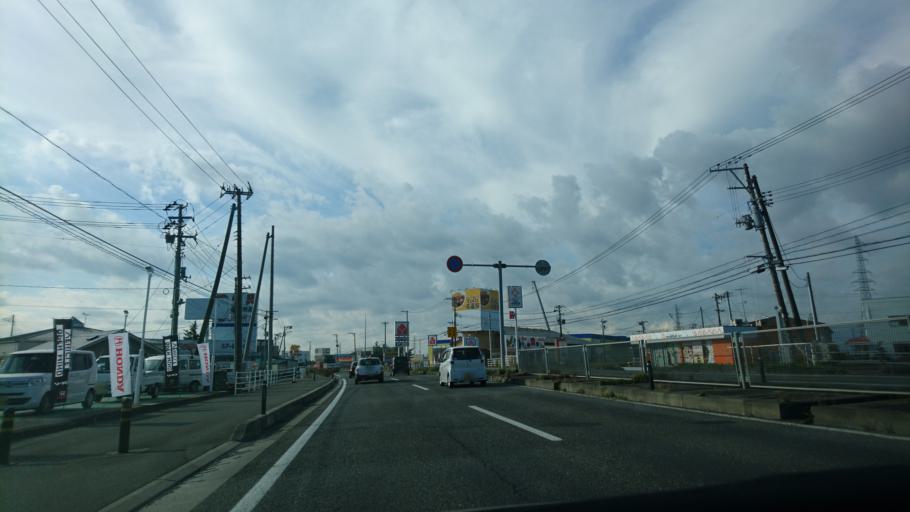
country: JP
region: Miyagi
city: Furukawa
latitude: 38.5819
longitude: 140.9463
